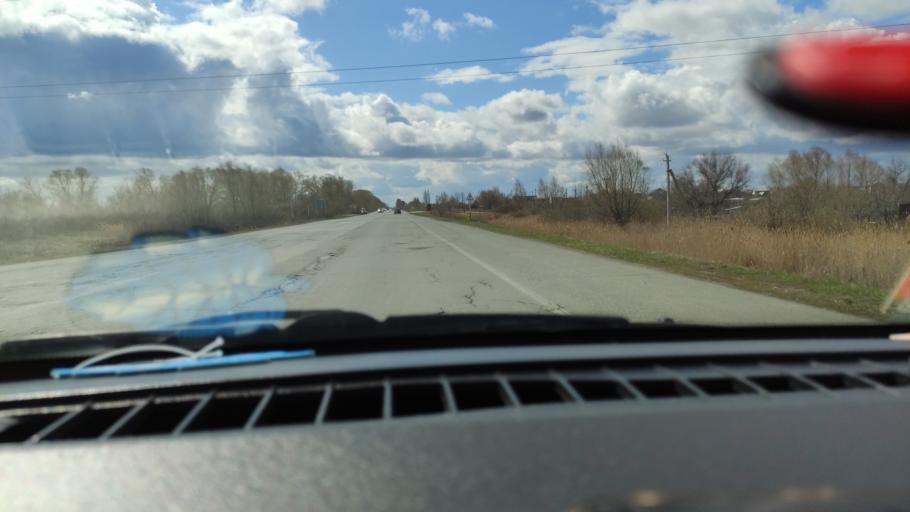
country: RU
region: Samara
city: Tol'yatti
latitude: 53.7057
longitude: 49.4221
